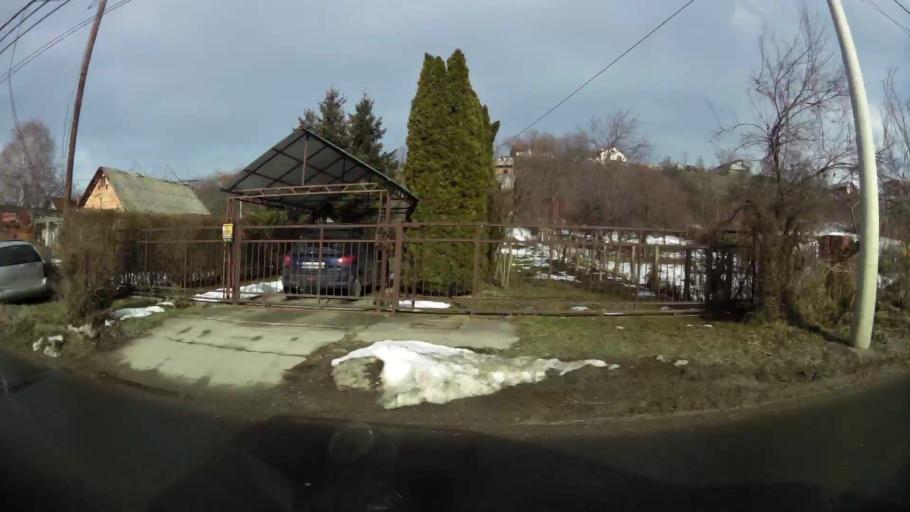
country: RS
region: Central Serbia
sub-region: Belgrade
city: Surcin
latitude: 44.7967
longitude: 20.3434
